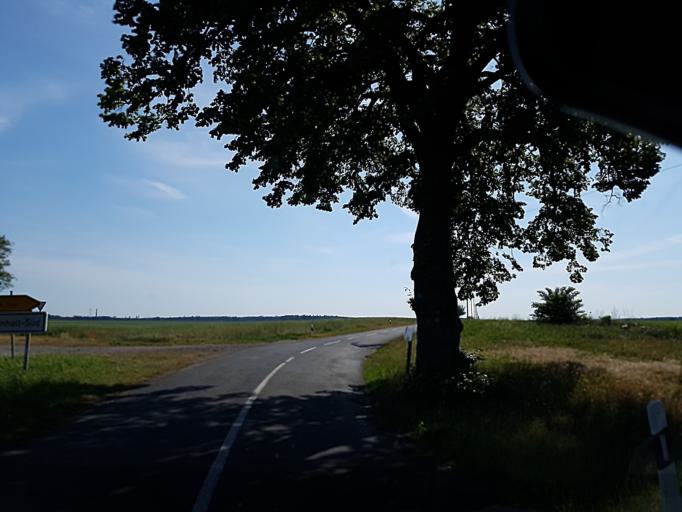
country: DE
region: Saxony-Anhalt
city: Lindau
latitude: 52.0343
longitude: 12.2494
